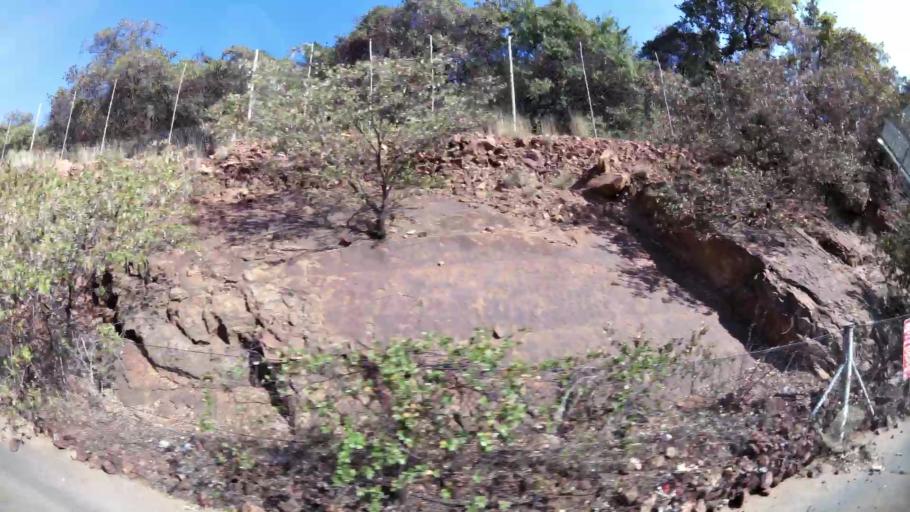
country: ZA
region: Gauteng
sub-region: City of Tshwane Metropolitan Municipality
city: Pretoria
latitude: -25.6887
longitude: 28.1950
